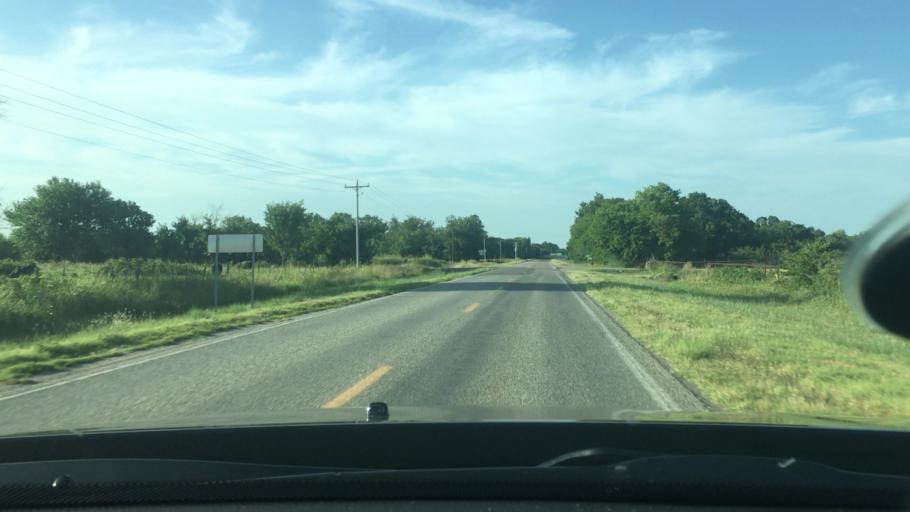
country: US
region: Oklahoma
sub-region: Pontotoc County
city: Ada
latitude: 34.5069
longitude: -96.6292
